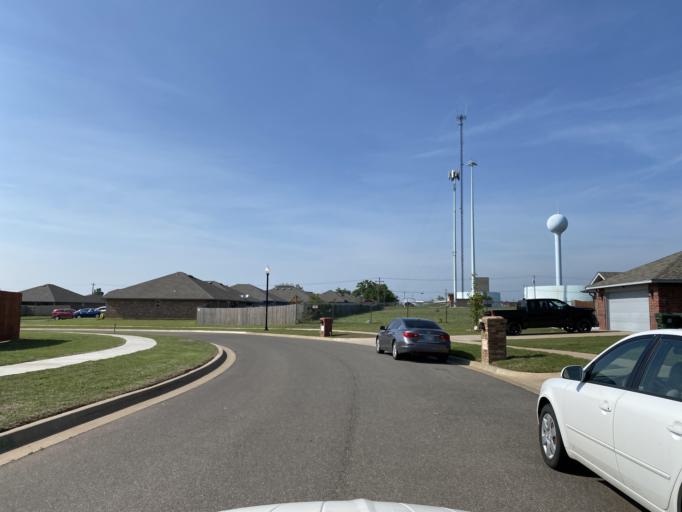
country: US
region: Oklahoma
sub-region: Oklahoma County
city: Nicoma Park
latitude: 35.4410
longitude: -97.3411
